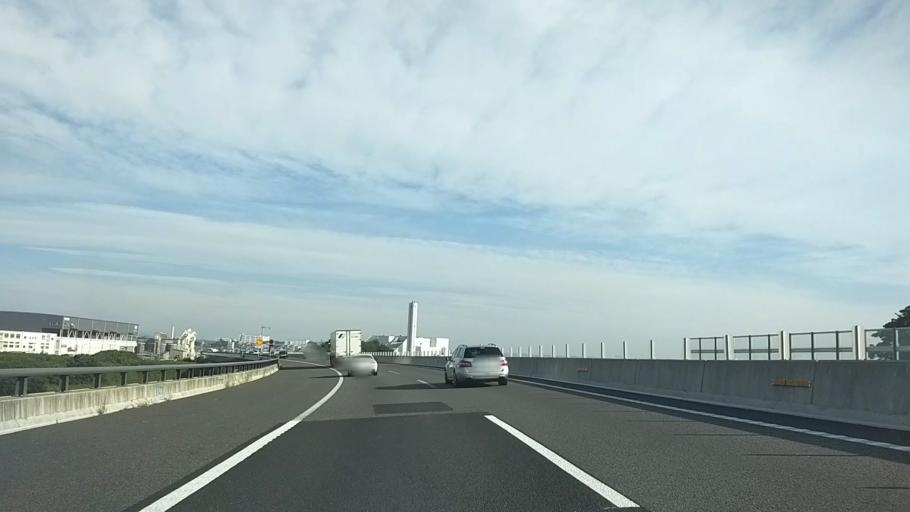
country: JP
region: Kanagawa
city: Atsugi
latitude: 35.4523
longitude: 139.3745
